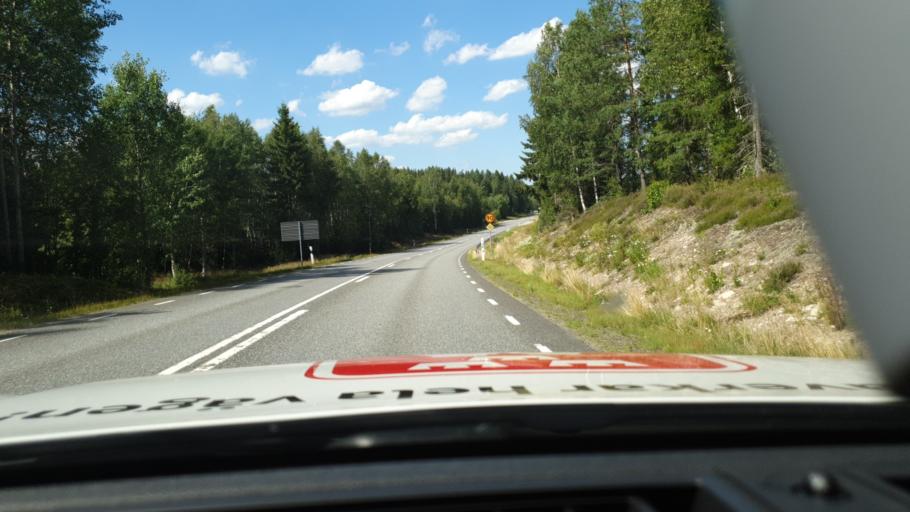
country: SE
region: Joenkoeping
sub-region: Vaggeryds Kommun
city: Vaggeryd
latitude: 57.5033
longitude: 14.2842
